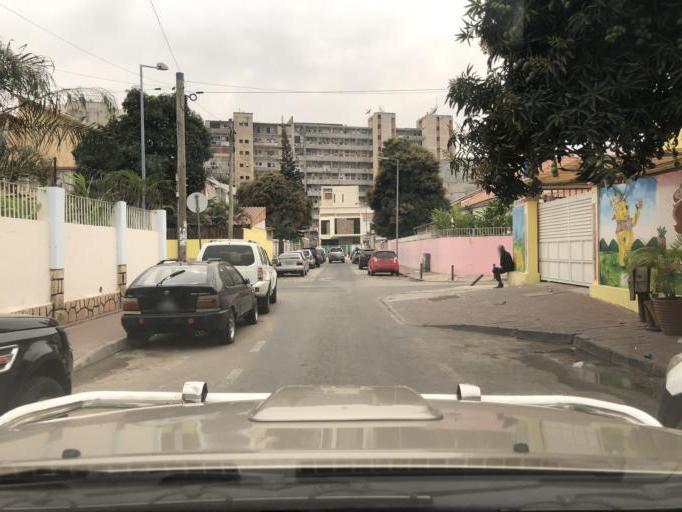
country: AO
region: Luanda
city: Luanda
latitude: -8.8202
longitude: 13.2484
